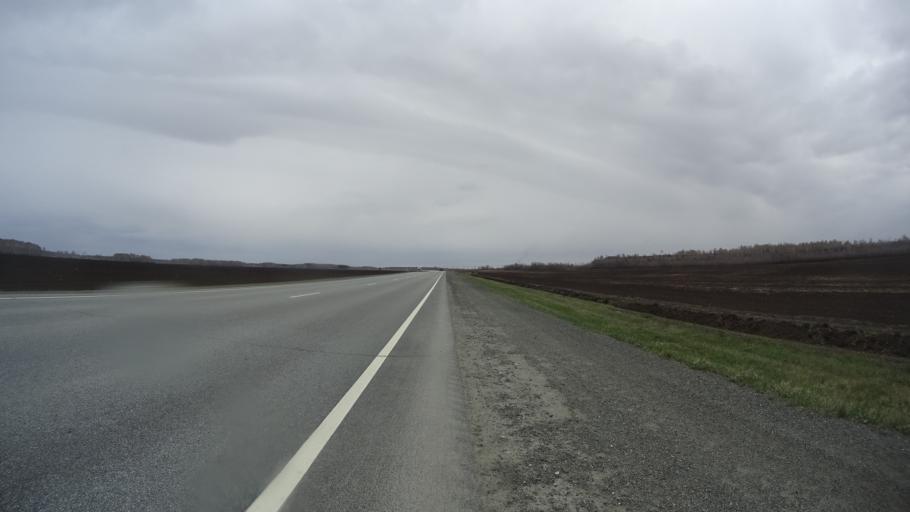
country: RU
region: Chelyabinsk
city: Krasnogorskiy
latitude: 54.5715
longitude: 61.2906
